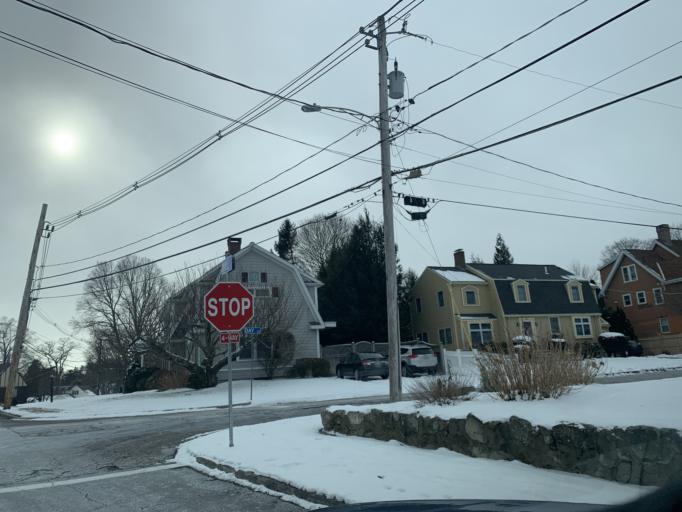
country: US
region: Massachusetts
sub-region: Norfolk County
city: Norwood
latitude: 42.1934
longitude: -71.2046
